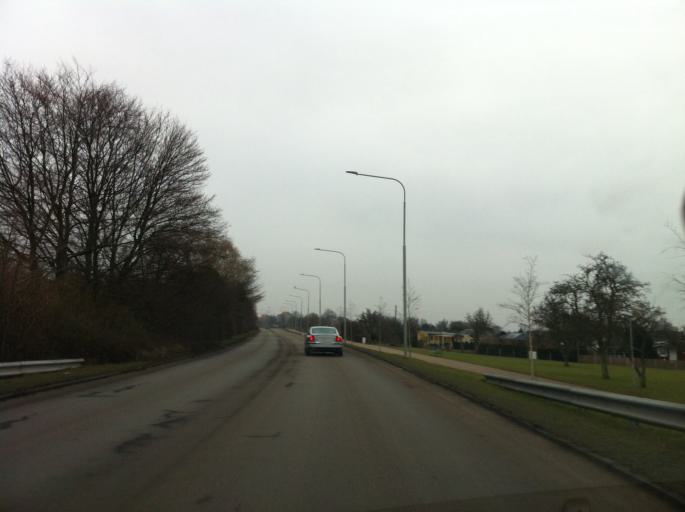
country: SE
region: Skane
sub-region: Landskrona
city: Landskrona
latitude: 55.8884
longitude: 12.8194
